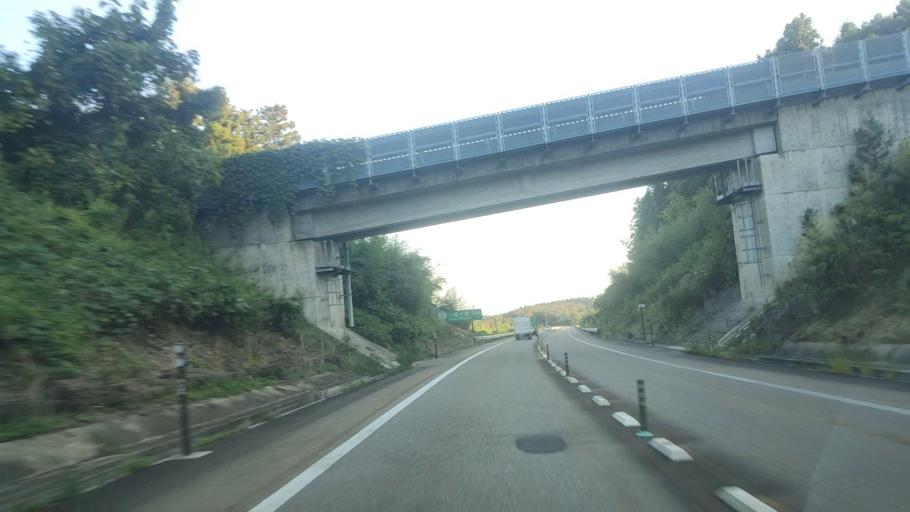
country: JP
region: Ishikawa
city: Nanao
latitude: 36.9919
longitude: 137.0466
